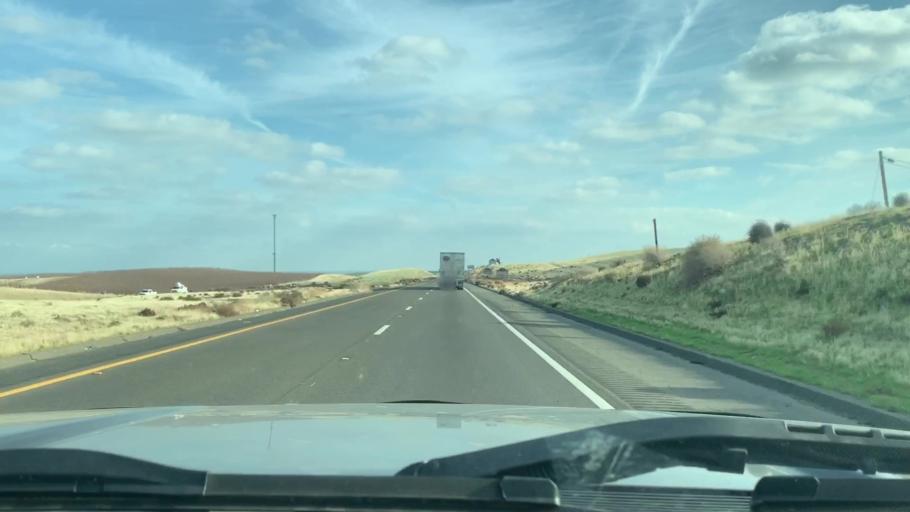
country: US
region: California
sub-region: Kings County
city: Kettleman City
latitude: 36.0180
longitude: -120.0036
